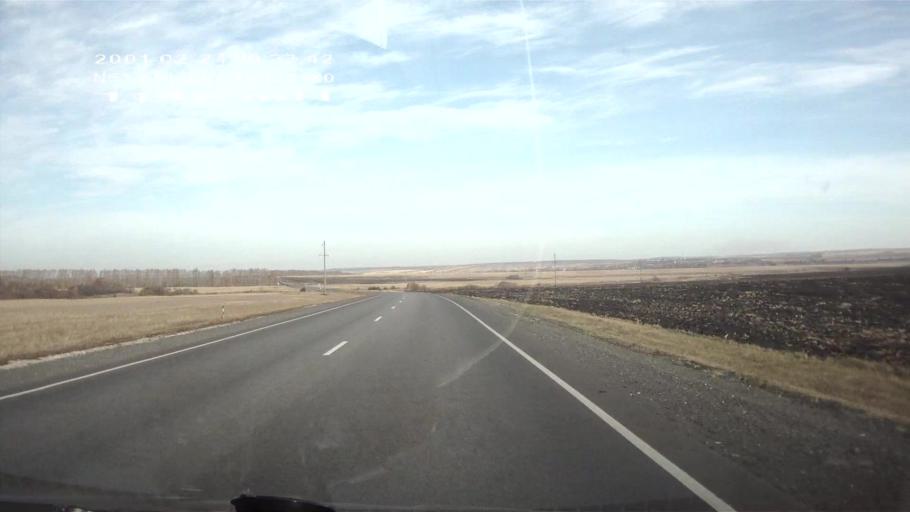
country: RU
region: Penza
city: Mokshan
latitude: 53.5746
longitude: 44.7288
